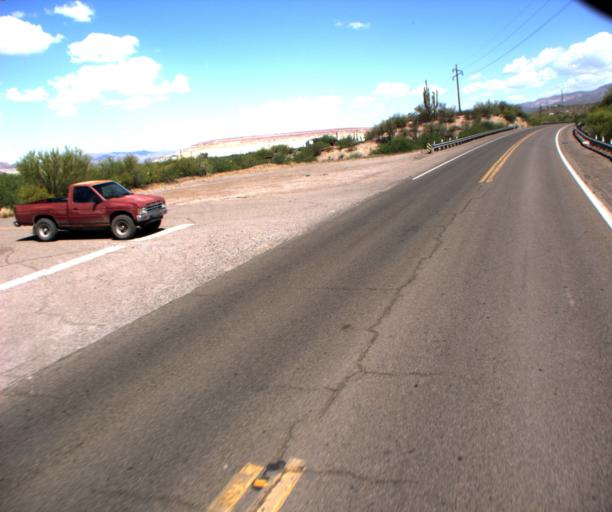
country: US
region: Arizona
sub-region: Pinal County
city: Kearny
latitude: 32.9775
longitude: -110.7680
